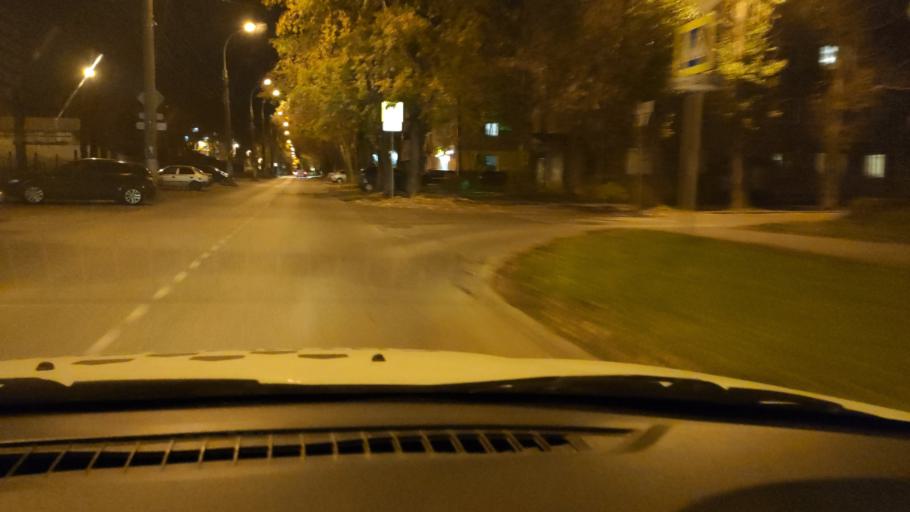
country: RU
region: Perm
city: Perm
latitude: 57.9844
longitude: 56.1894
